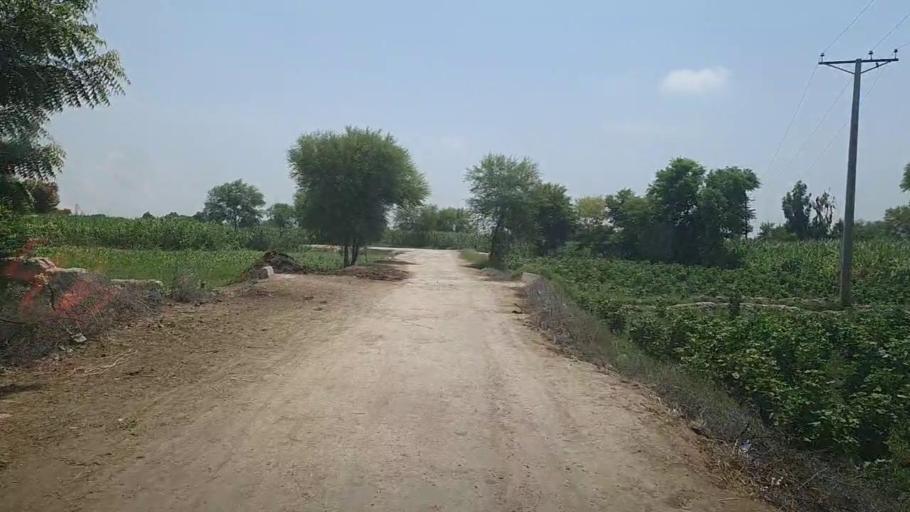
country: PK
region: Sindh
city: Ubauro
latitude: 28.2393
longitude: 69.8169
